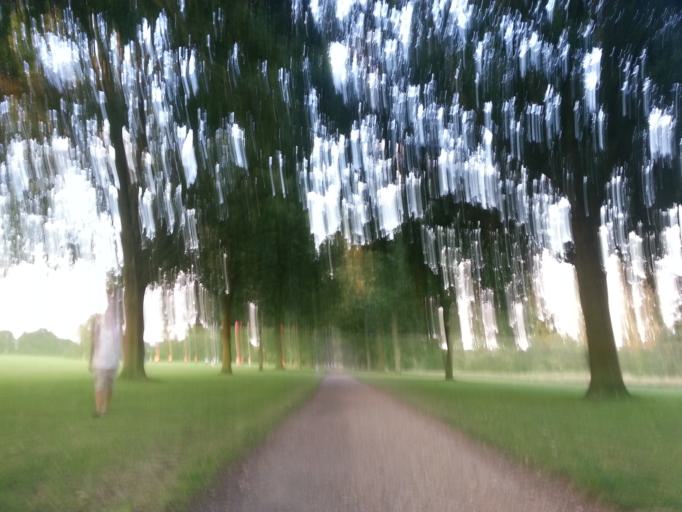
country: GB
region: England
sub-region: Suffolk
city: Ipswich
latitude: 52.0339
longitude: 1.1377
